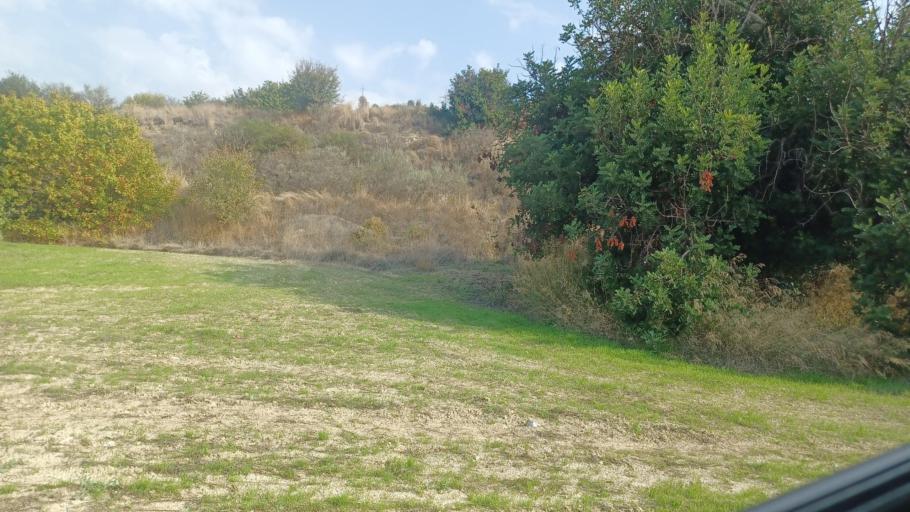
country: CY
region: Pafos
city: Polis
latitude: 34.9719
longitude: 32.4553
